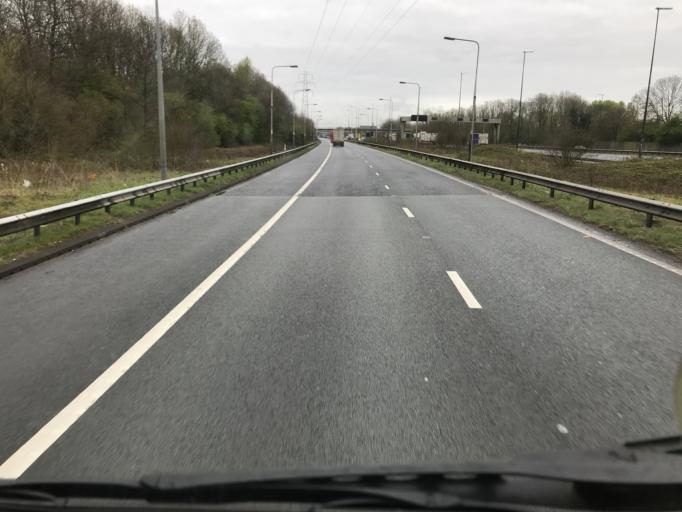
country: GB
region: England
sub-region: Warrington
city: Croft
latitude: 53.4213
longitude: -2.5476
